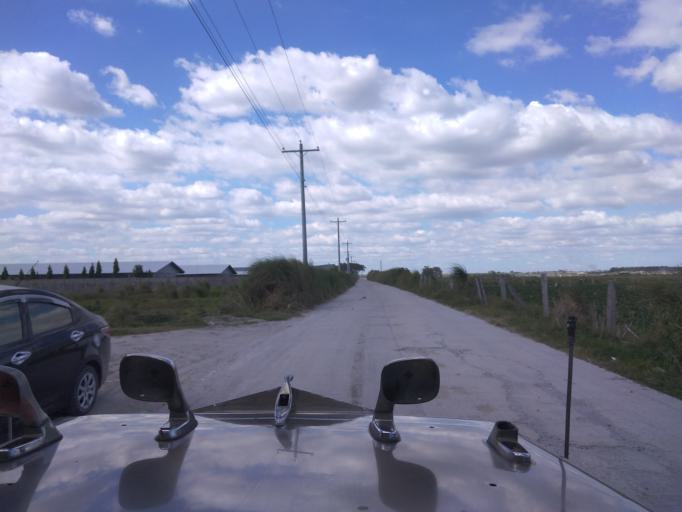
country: PH
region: Central Luzon
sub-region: Province of Pampanga
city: Magliman
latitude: 15.0443
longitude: 120.6287
